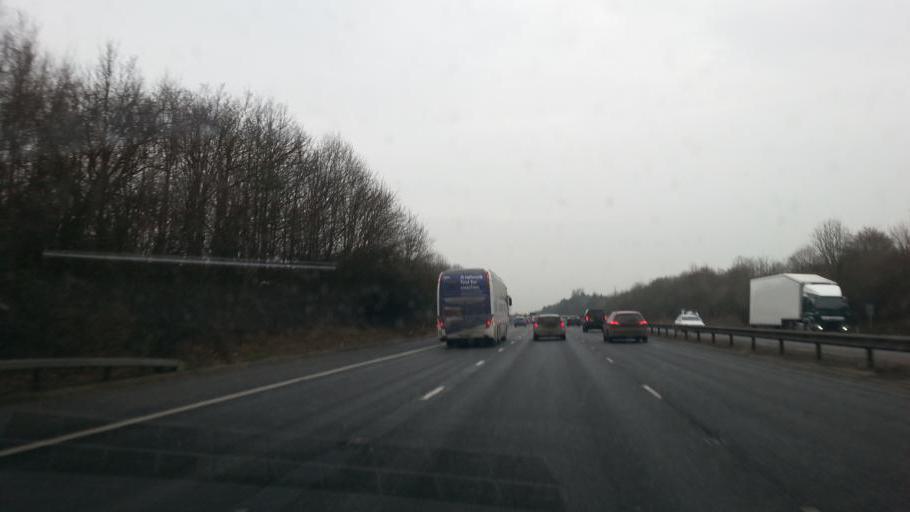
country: GB
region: England
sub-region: Hertfordshire
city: Sawbridgeworth
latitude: 51.7772
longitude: 0.1644
